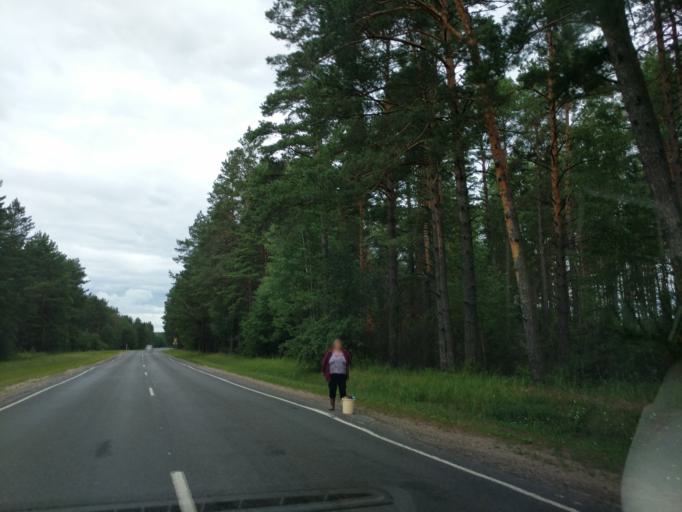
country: BY
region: Minsk
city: Myadzyel
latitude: 54.8377
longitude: 26.9328
